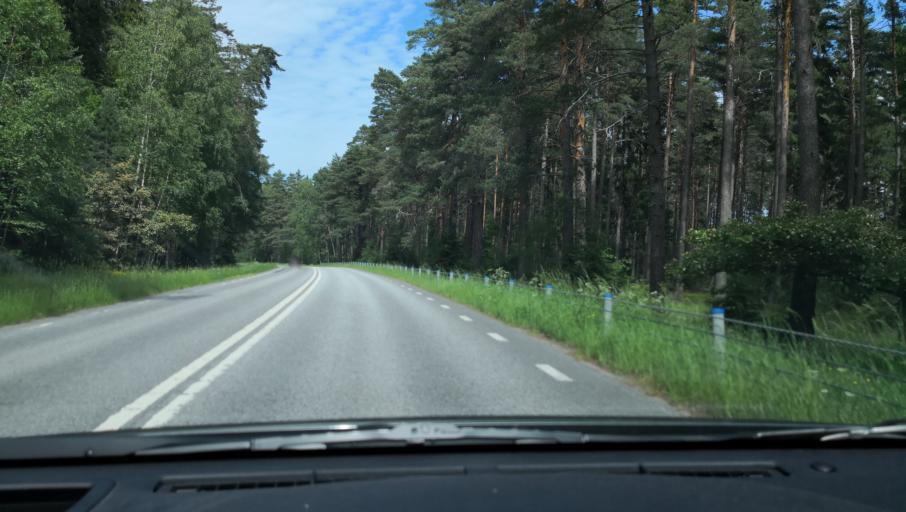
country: SE
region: Uppsala
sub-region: Uppsala Kommun
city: Saevja
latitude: 59.7745
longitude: 17.6608
